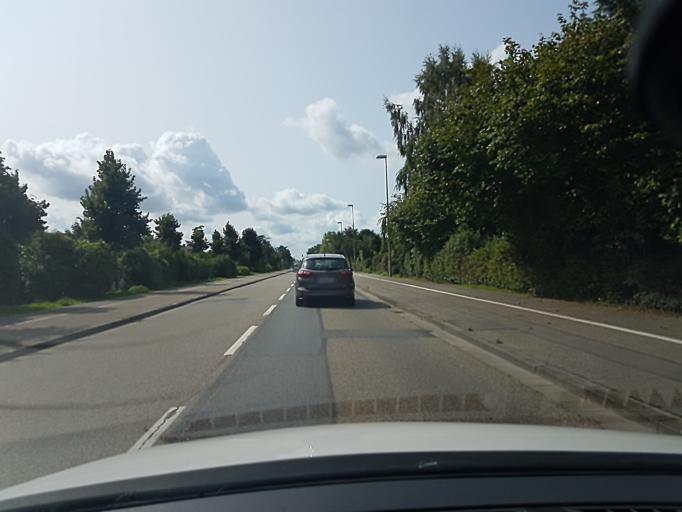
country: DE
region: Rheinland-Pfalz
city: Otterstadt
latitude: 49.3491
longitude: 8.4329
